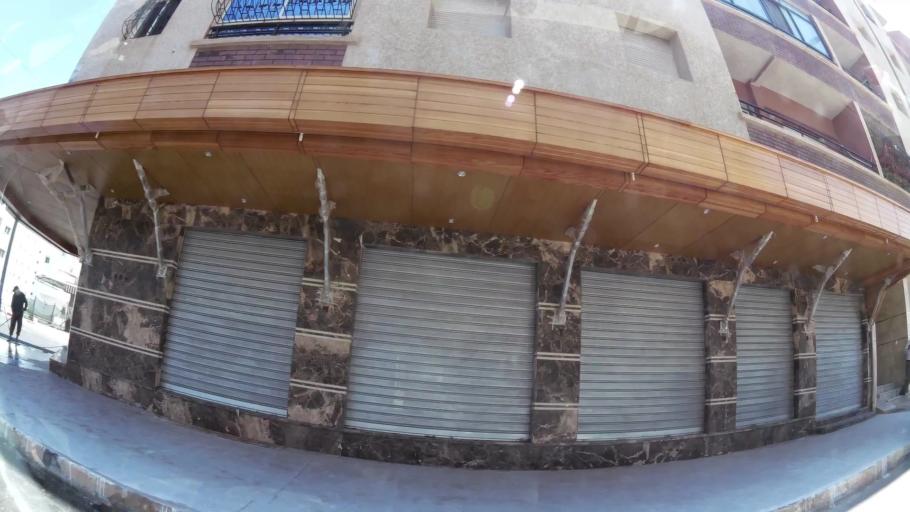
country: MA
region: Rabat-Sale-Zemmour-Zaer
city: Sale
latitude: 34.0814
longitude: -6.7862
